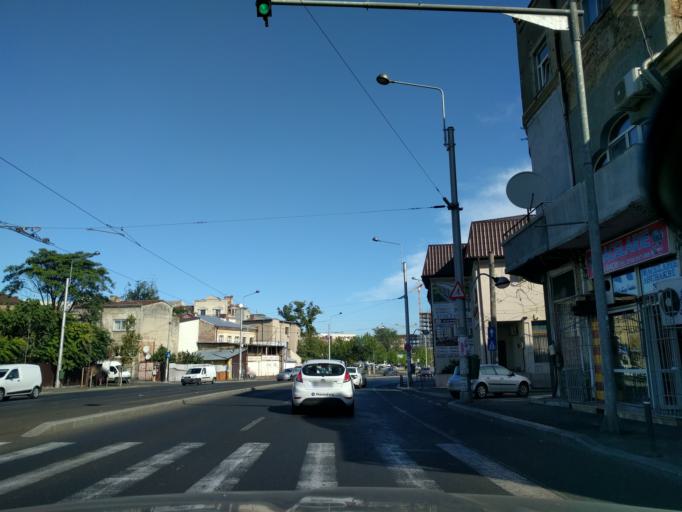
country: RO
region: Bucuresti
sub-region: Municipiul Bucuresti
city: Bucuresti
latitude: 44.4417
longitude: 26.0810
